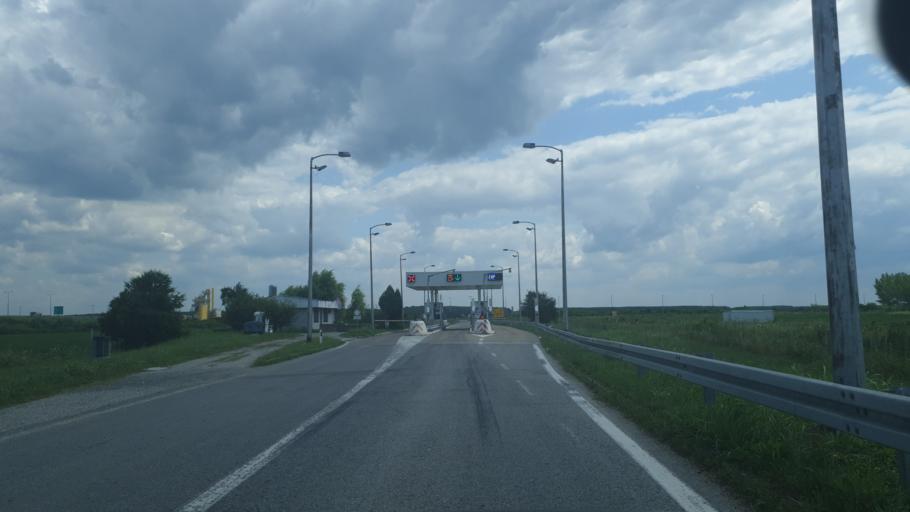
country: RS
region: Autonomna Pokrajina Vojvodina
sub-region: Sremski Okrug
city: Sid
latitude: 45.0460
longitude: 19.2091
